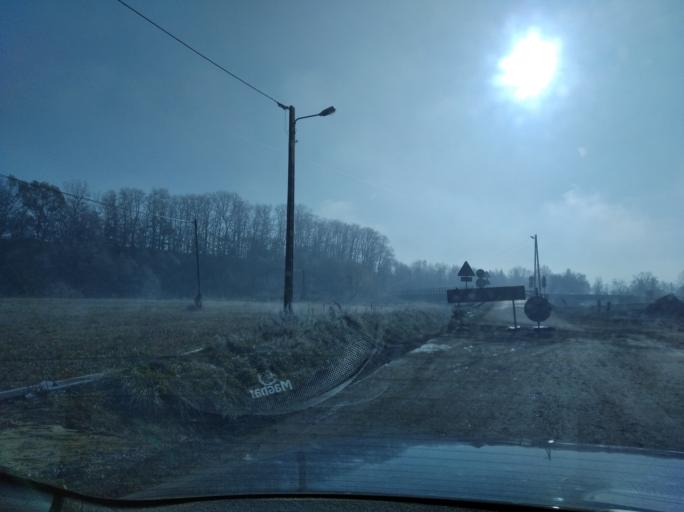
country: PL
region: Subcarpathian Voivodeship
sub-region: Powiat strzyzowski
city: Wysoka Strzyzowska
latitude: 49.8659
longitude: 21.7069
